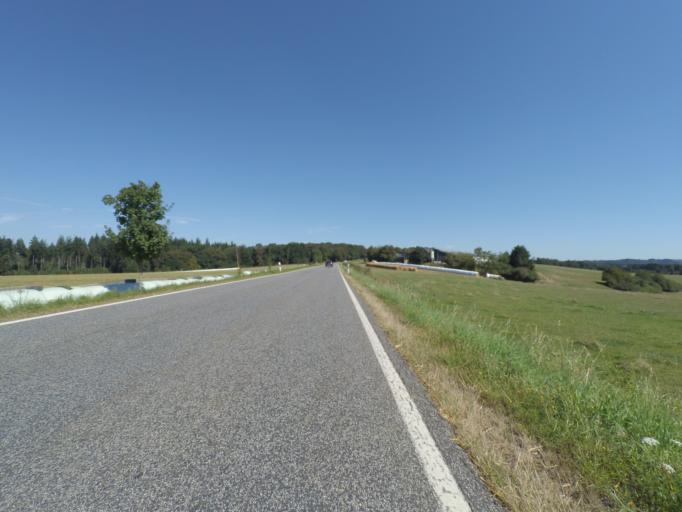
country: DE
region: Rheinland-Pfalz
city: Filz
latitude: 50.1618
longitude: 6.9878
